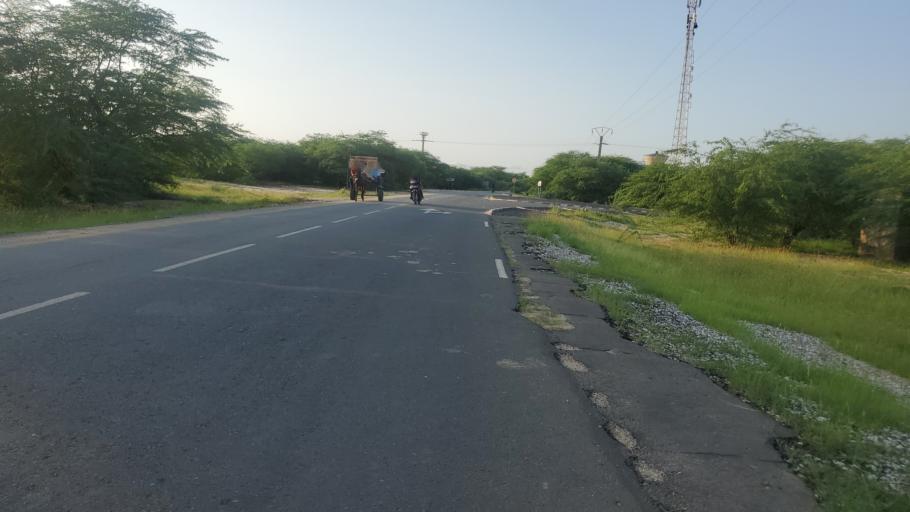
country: SN
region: Saint-Louis
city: Saint-Louis
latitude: 16.2048
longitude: -16.4143
